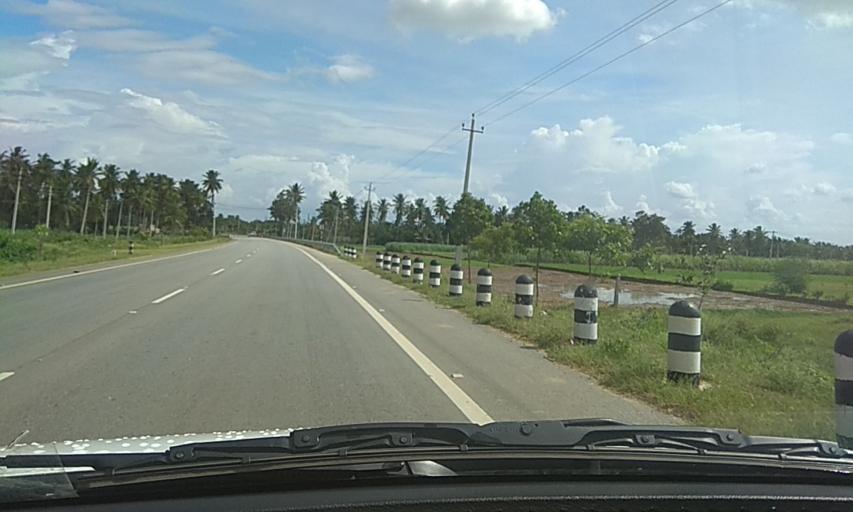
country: IN
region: Karnataka
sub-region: Mandya
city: Maddur
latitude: 12.6536
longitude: 77.0530
